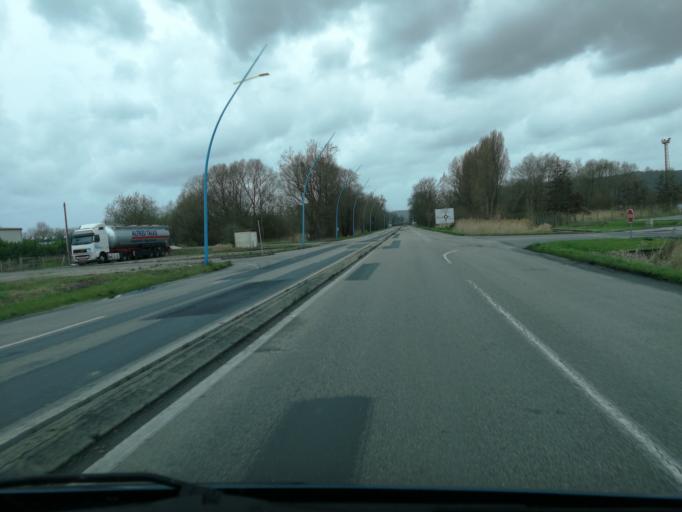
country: FR
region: Haute-Normandie
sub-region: Departement de l'Eure
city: Quillebeuf-sur-Seine
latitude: 49.4813
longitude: 0.5329
